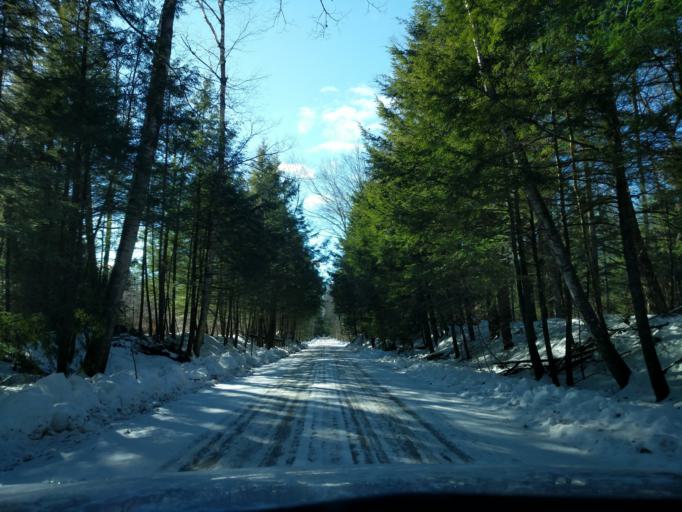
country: US
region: Wisconsin
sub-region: Menominee County
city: Keshena
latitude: 45.0951
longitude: -88.6162
